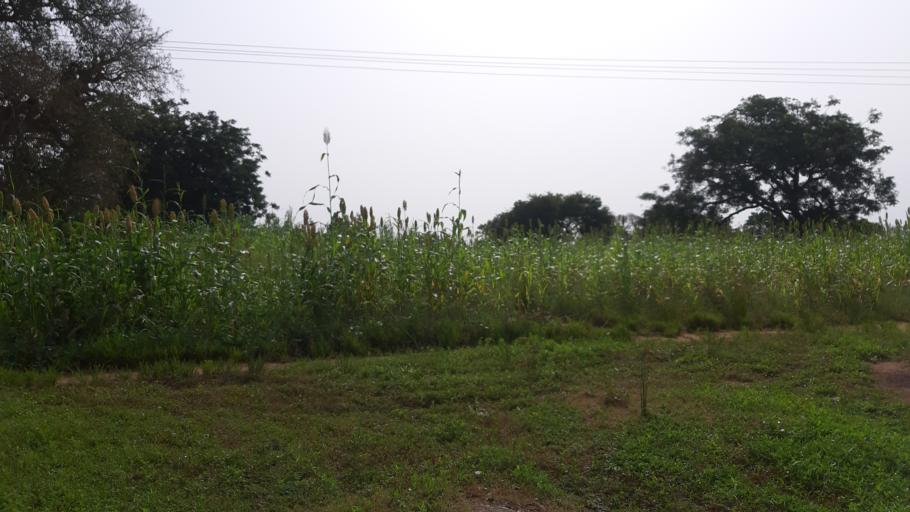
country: GH
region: Upper East
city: Bolgatanga
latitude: 10.7822
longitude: -0.7870
